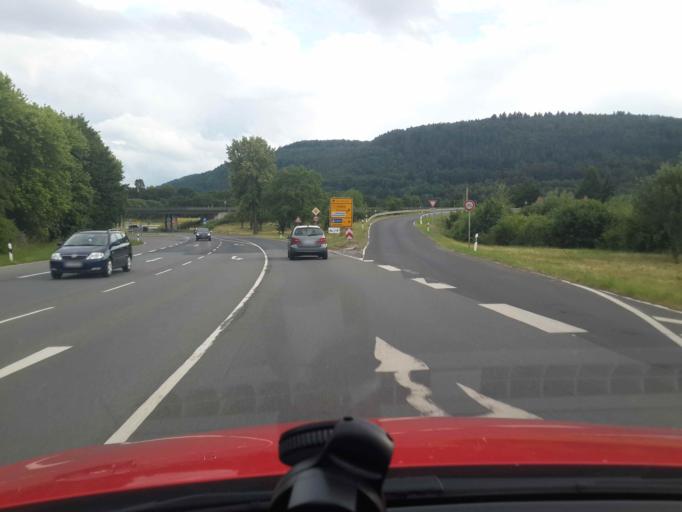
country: DE
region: Bavaria
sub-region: Regierungsbezirk Unterfranken
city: Kleinheubach
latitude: 49.7131
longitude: 9.2181
